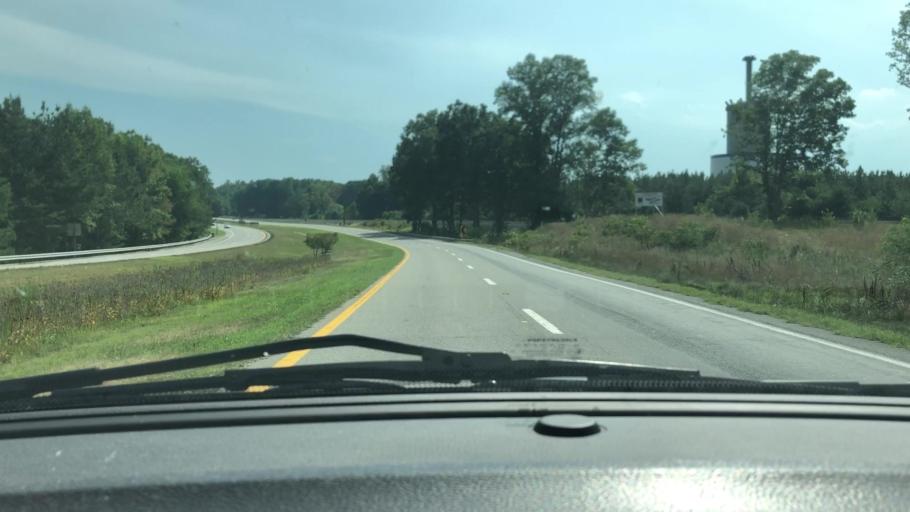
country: US
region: North Carolina
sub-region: Rockingham County
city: Stoneville
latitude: 36.5448
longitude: -79.9079
